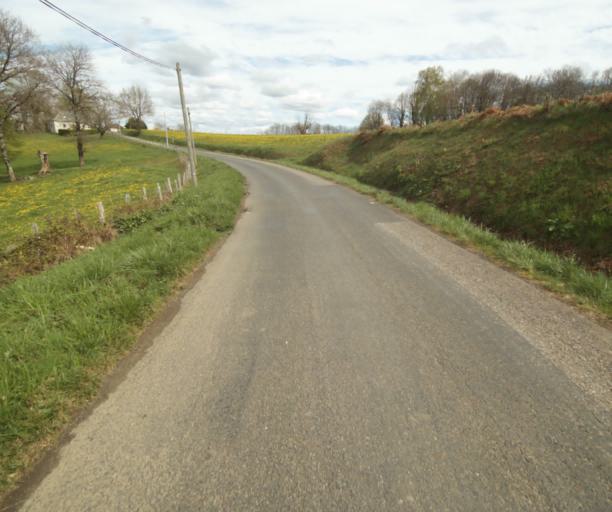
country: FR
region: Limousin
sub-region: Departement de la Correze
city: Laguenne
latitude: 45.2381
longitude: 1.8368
